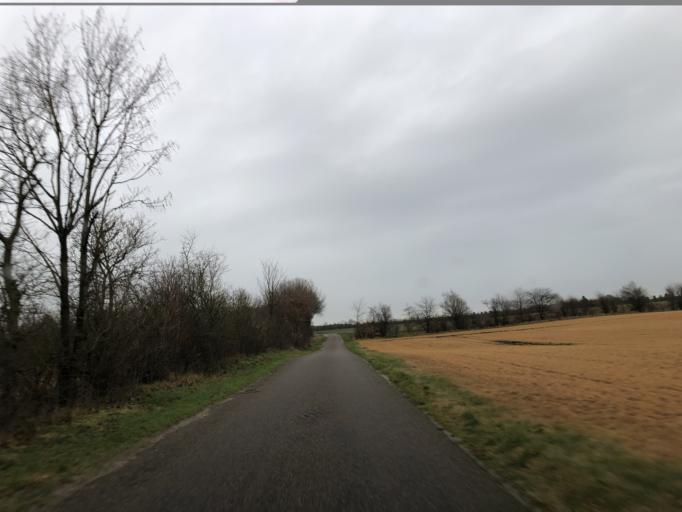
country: DK
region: Central Jutland
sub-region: Holstebro Kommune
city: Vinderup
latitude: 56.3766
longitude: 8.8588
